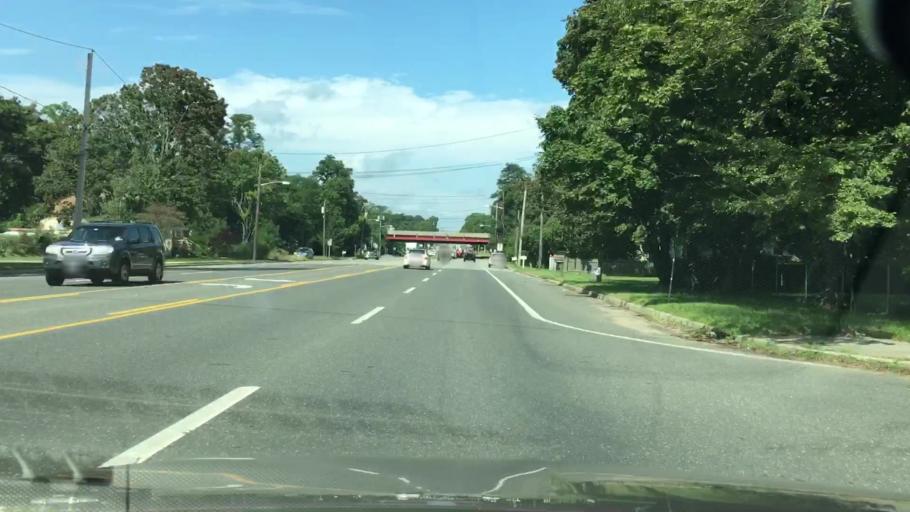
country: US
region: New York
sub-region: Suffolk County
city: Ronkonkoma
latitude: 40.8095
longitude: -73.1245
